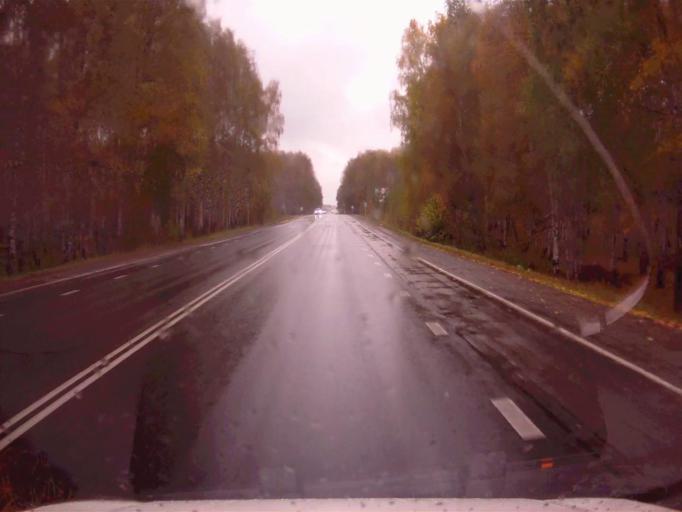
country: RU
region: Chelyabinsk
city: Argayash
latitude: 55.4125
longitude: 61.0382
